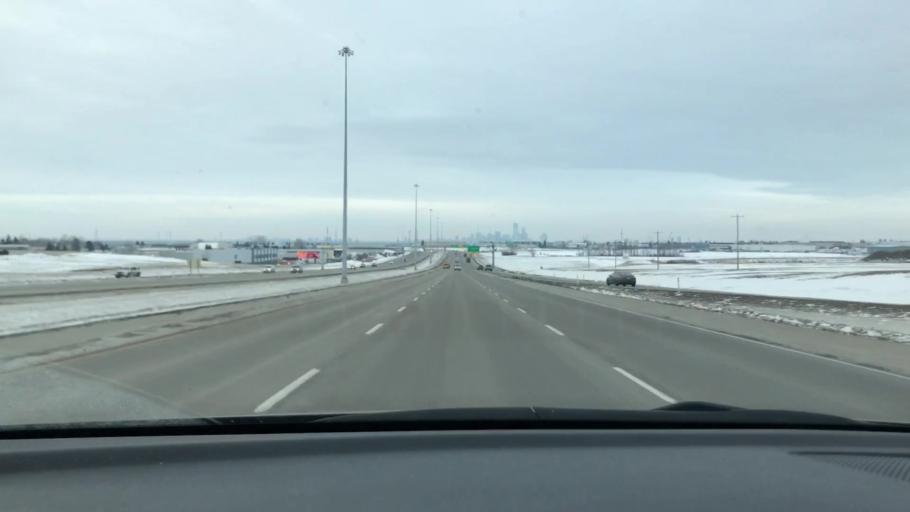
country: CA
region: Alberta
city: Sherwood Park
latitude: 53.5140
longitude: -113.3494
